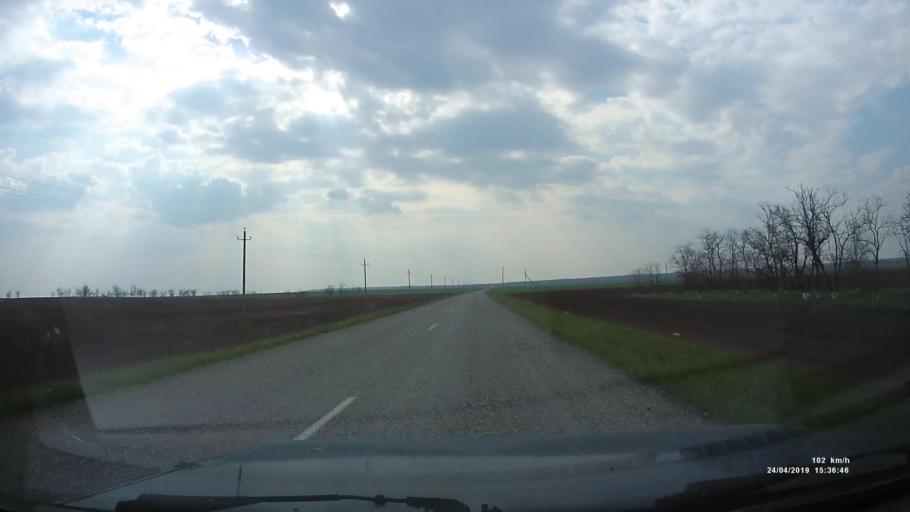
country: RU
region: Kalmykiya
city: Yashalta
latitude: 46.5991
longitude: 42.8621
